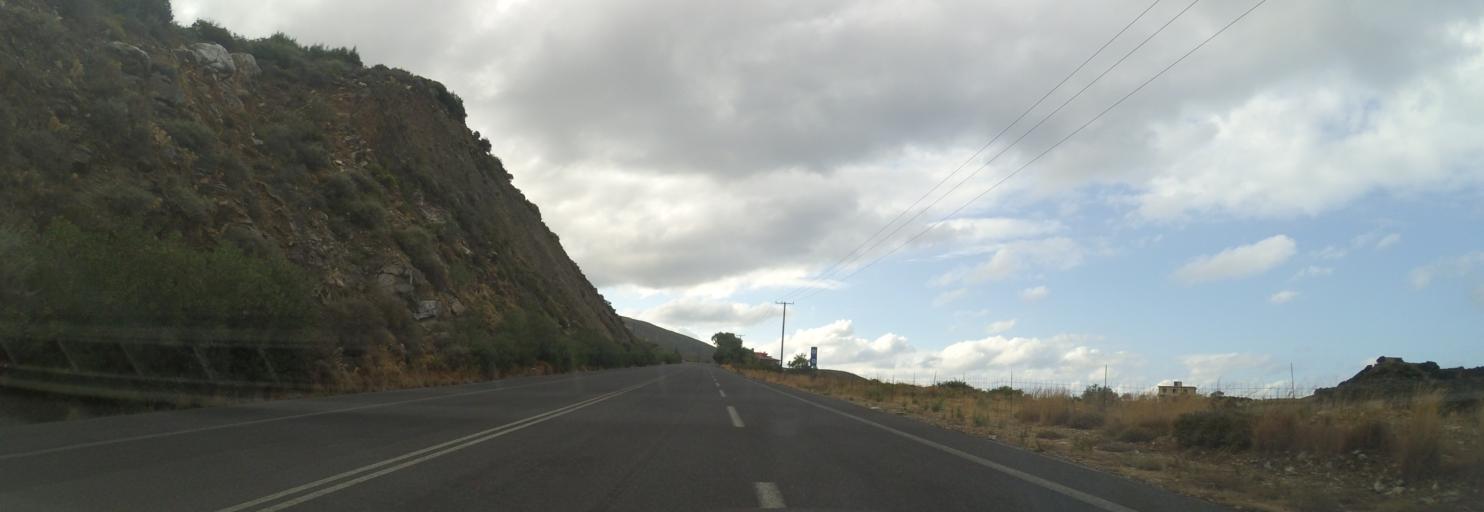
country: GR
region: Crete
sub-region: Nomos Rethymnis
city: Perama
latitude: 35.4088
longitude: 24.7739
